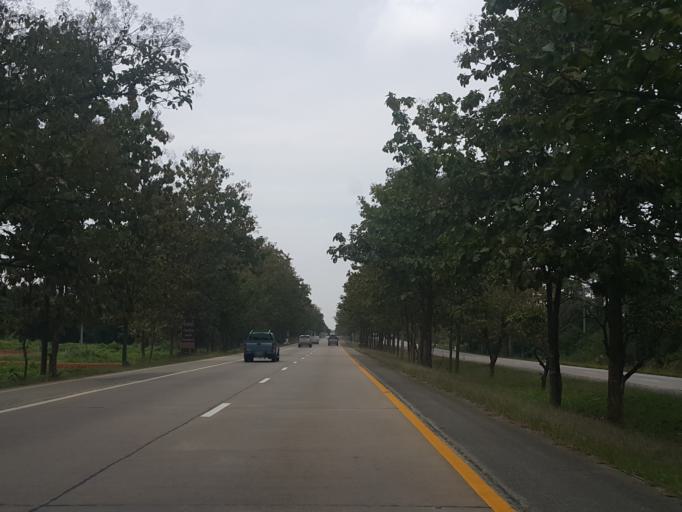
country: TH
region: Lamphun
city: Mae Tha
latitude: 18.5157
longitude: 99.0924
